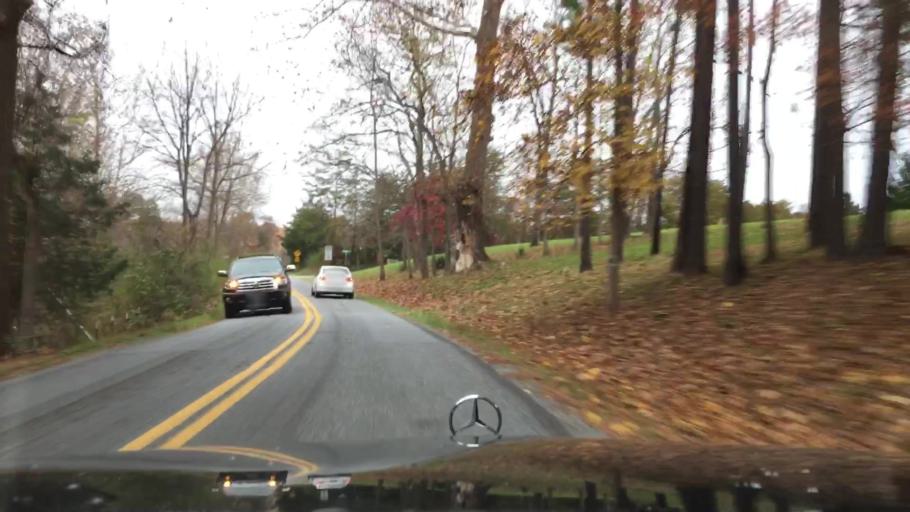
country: US
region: Virginia
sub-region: Campbell County
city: Timberlake
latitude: 37.2819
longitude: -79.2712
